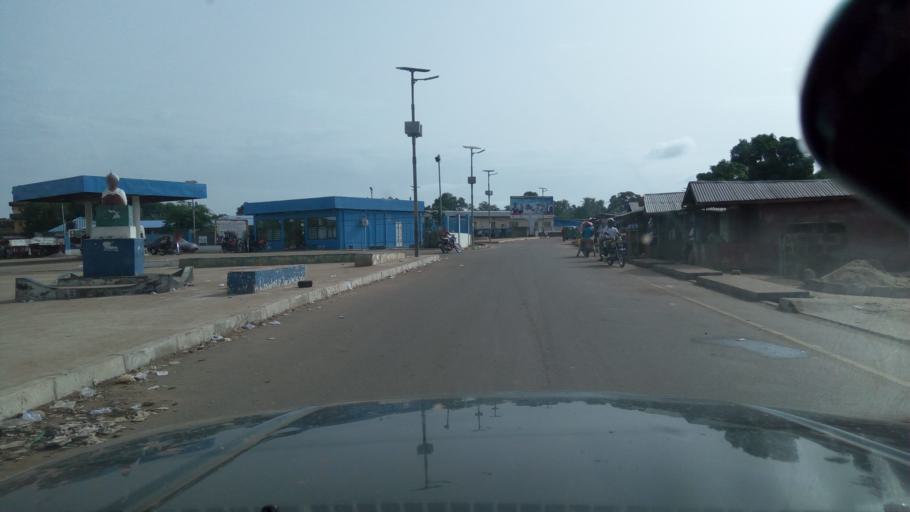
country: SL
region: Northern Province
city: Port Loko
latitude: 8.7639
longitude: -12.7854
